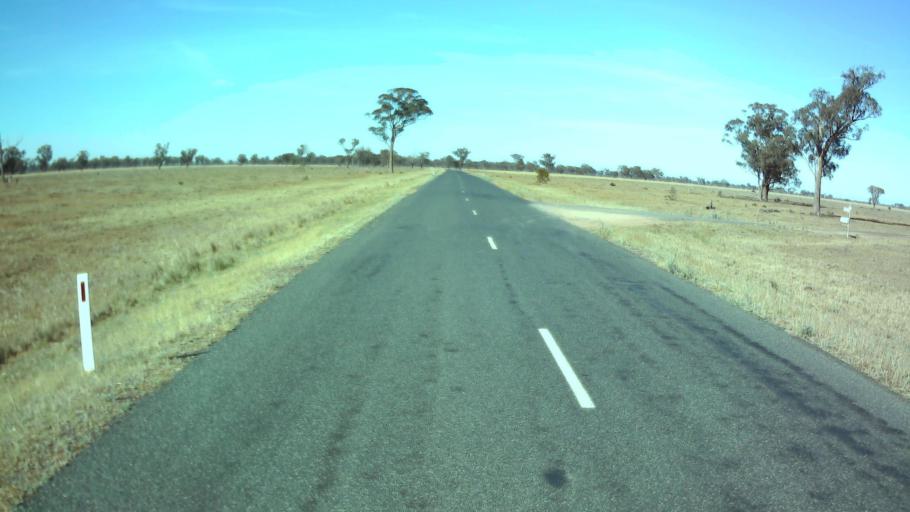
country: AU
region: New South Wales
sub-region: Weddin
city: Grenfell
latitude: -34.0481
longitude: 147.9217
